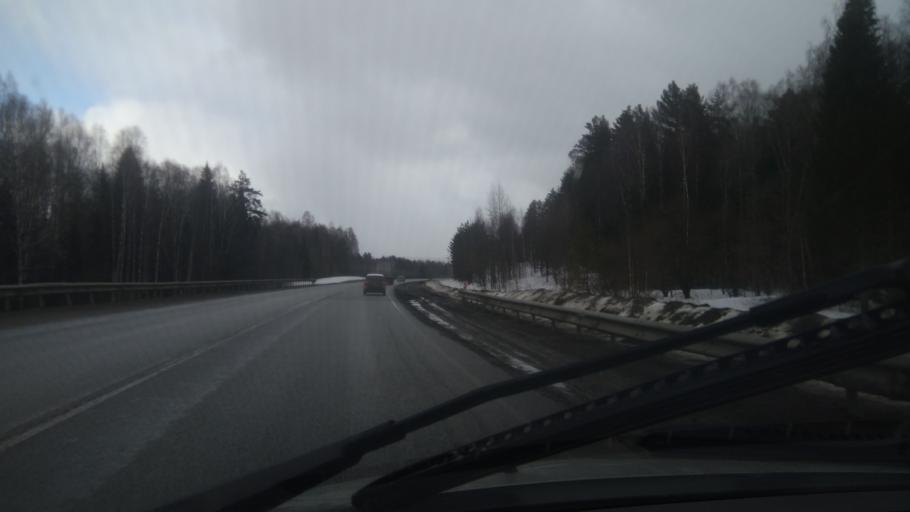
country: RU
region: Sverdlovsk
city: Ufimskiy
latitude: 56.7869
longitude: 58.3835
